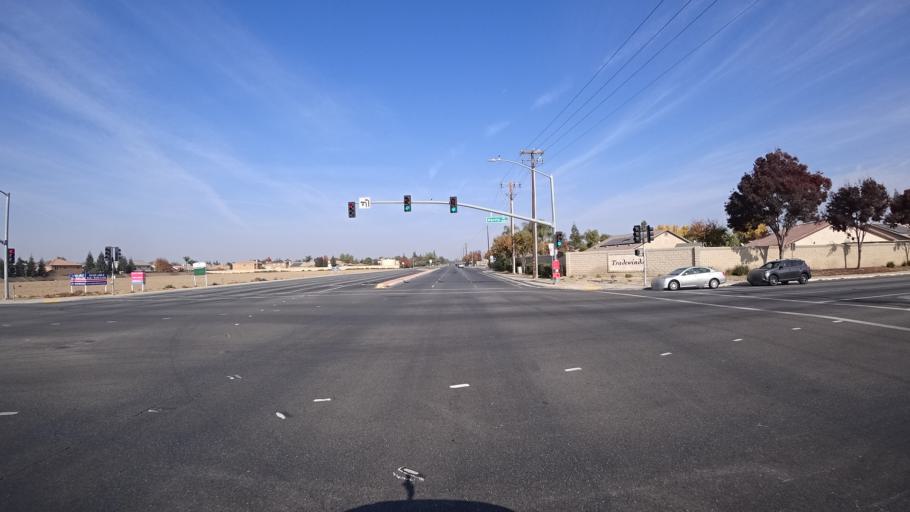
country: US
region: California
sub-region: Kern County
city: Greenacres
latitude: 35.3034
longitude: -119.1098
